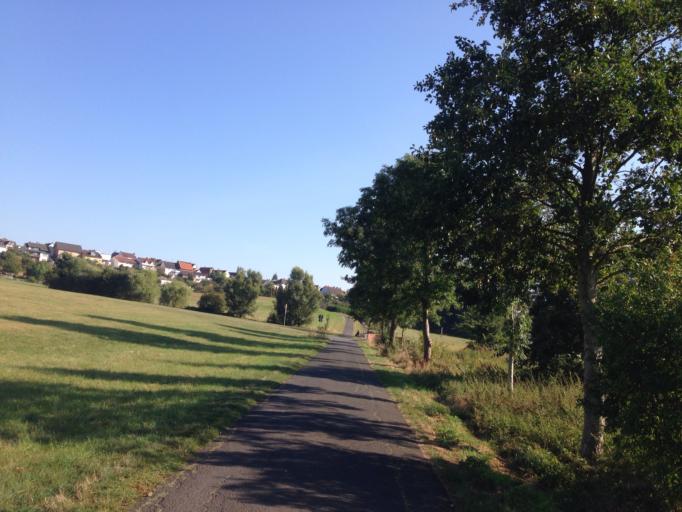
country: DE
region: Hesse
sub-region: Regierungsbezirk Giessen
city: Giessen
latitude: 50.5398
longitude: 8.7140
